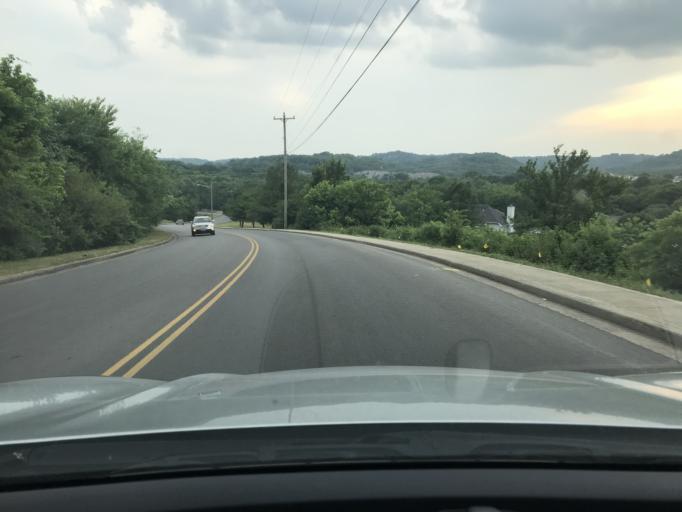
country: US
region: Tennessee
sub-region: Davidson County
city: Goodlettsville
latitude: 36.2983
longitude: -86.7159
